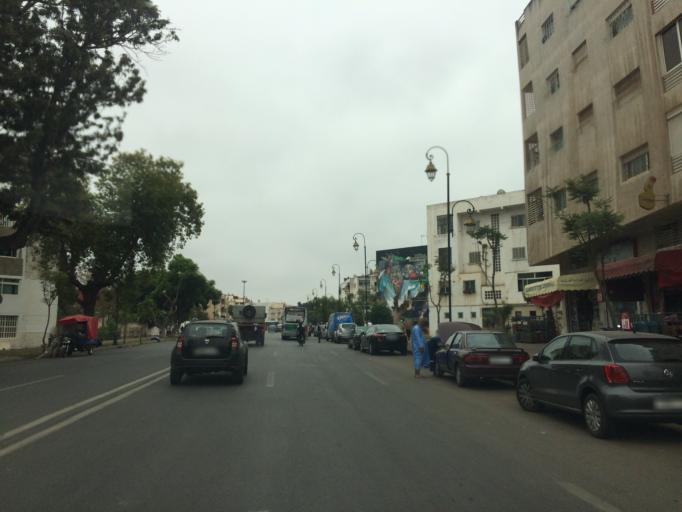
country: MA
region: Rabat-Sale-Zemmour-Zaer
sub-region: Rabat
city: Rabat
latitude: 33.9954
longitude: -6.8202
